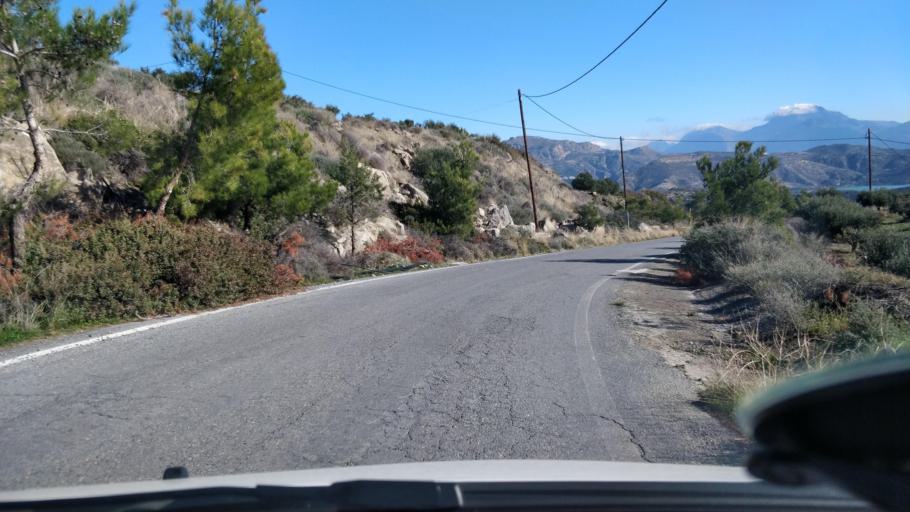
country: GR
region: Crete
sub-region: Nomos Lasithiou
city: Gra Liyia
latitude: 35.0354
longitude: 25.6607
